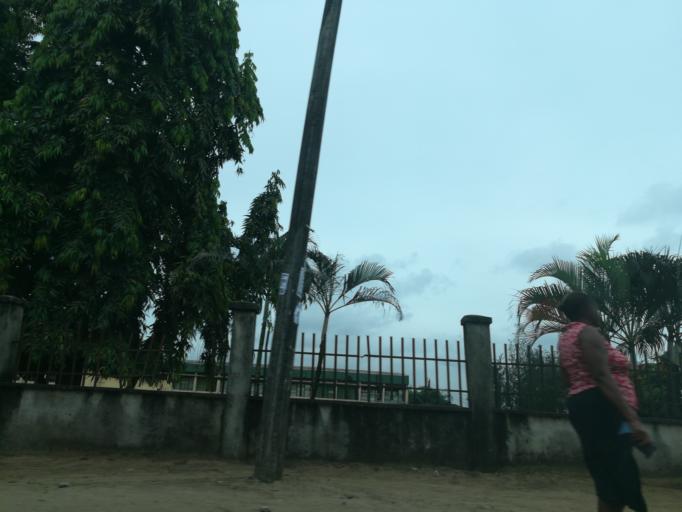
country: NG
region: Rivers
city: Port Harcourt
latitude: 4.8125
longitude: 6.9844
